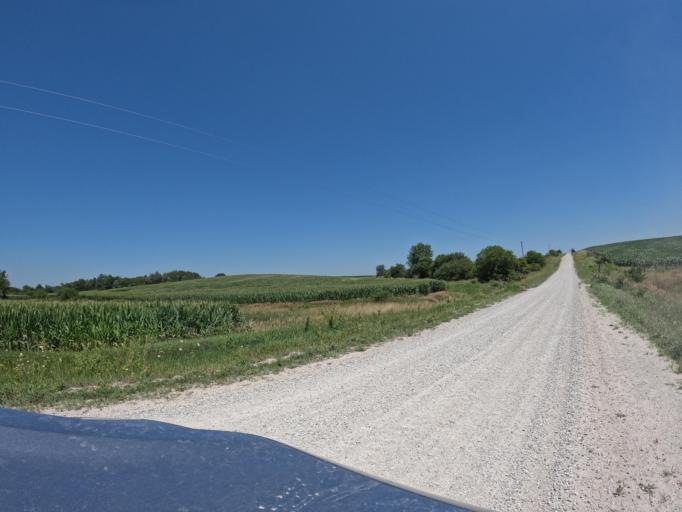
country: US
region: Iowa
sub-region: Keokuk County
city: Sigourney
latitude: 41.4234
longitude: -92.3412
